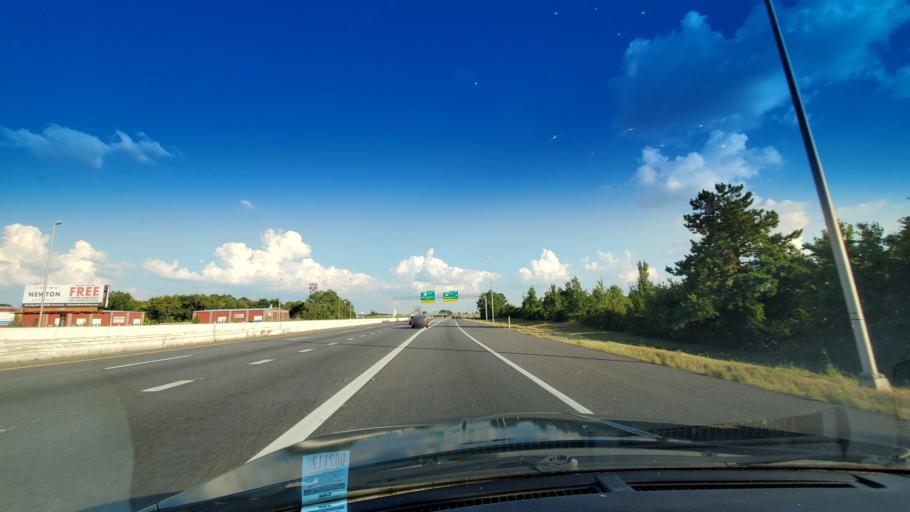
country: US
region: Tennessee
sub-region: Rutherford County
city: Murfreesboro
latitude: 35.8164
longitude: -86.4015
